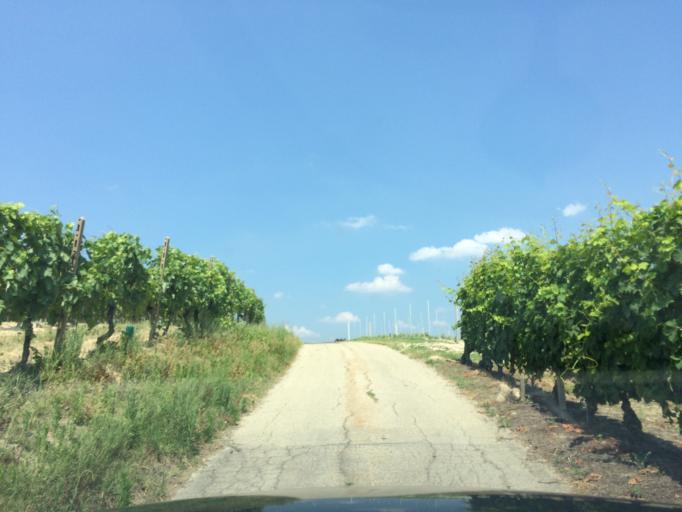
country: IT
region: Piedmont
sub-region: Provincia di Asti
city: Moasca
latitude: 44.7643
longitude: 8.2625
